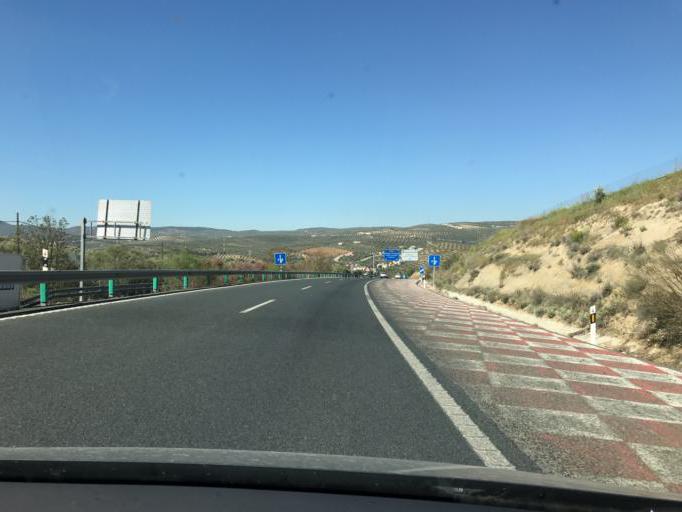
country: ES
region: Andalusia
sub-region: Provincia de Granada
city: Loja
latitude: 37.1587
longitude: -4.1990
